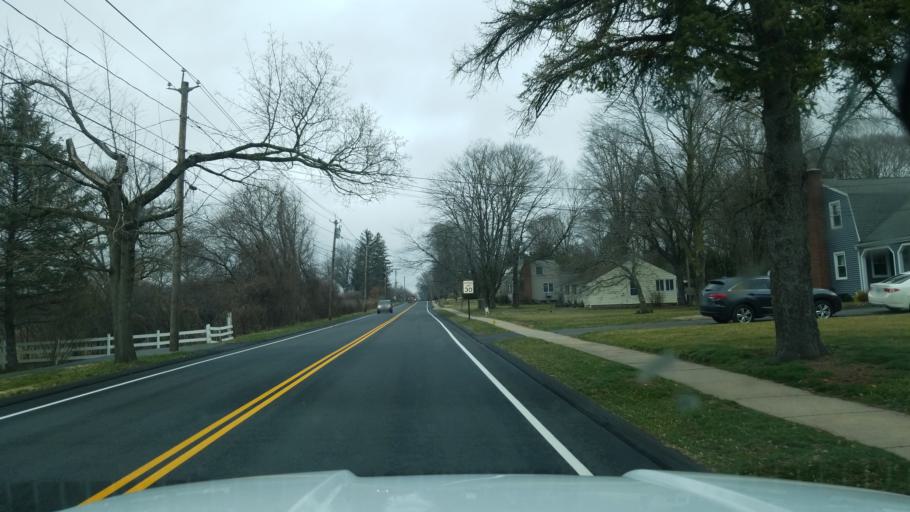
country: US
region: Connecticut
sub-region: Hartford County
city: Kensington
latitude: 41.6200
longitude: -72.7553
